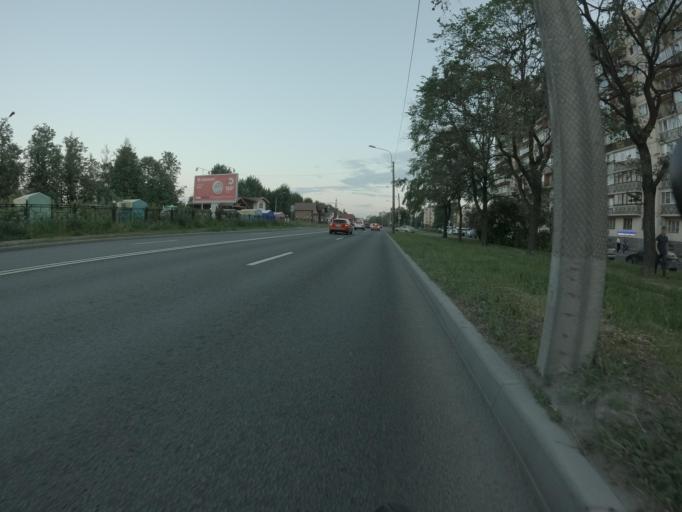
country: RU
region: St.-Petersburg
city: Dachnoye
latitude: 59.8444
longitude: 30.2784
